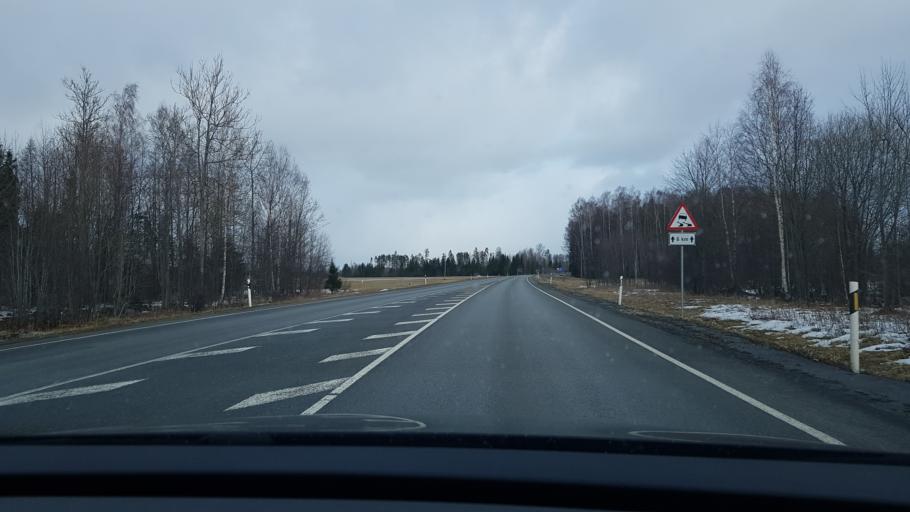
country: EE
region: Paernumaa
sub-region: Vaendra vald (alev)
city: Vandra
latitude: 58.6201
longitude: 24.9267
